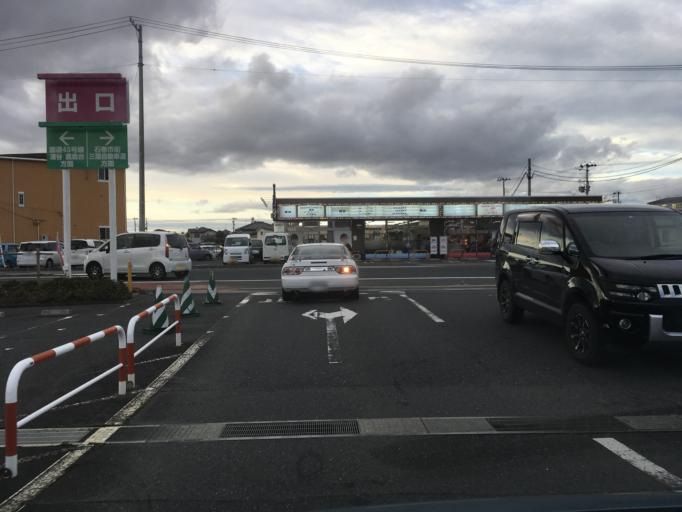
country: JP
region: Miyagi
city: Ishinomaki
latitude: 38.4493
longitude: 141.2661
